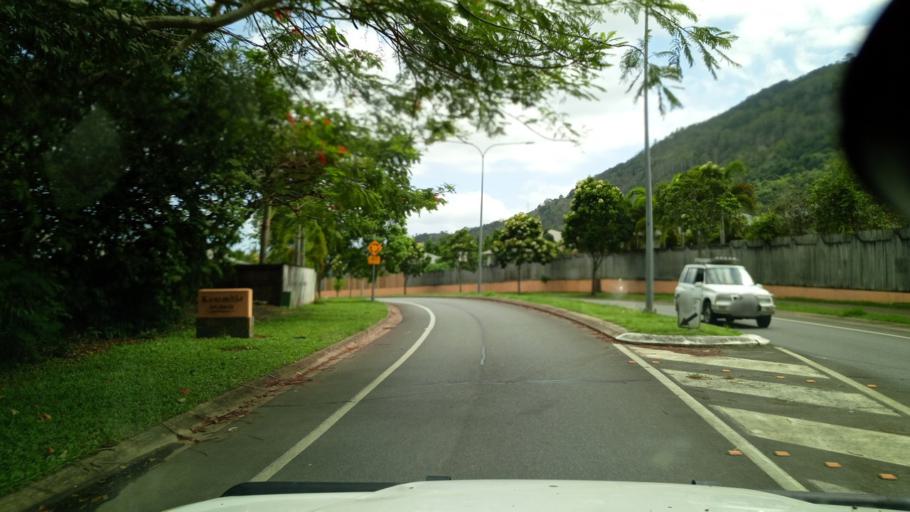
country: AU
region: Queensland
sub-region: Cairns
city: Redlynch
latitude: -16.9175
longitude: 145.7211
